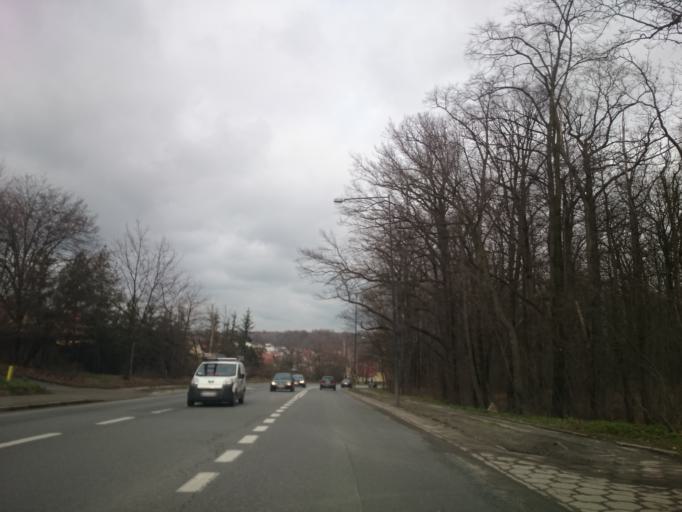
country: PL
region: Opole Voivodeship
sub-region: Powiat nyski
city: Nysa
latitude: 50.4801
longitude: 17.3052
